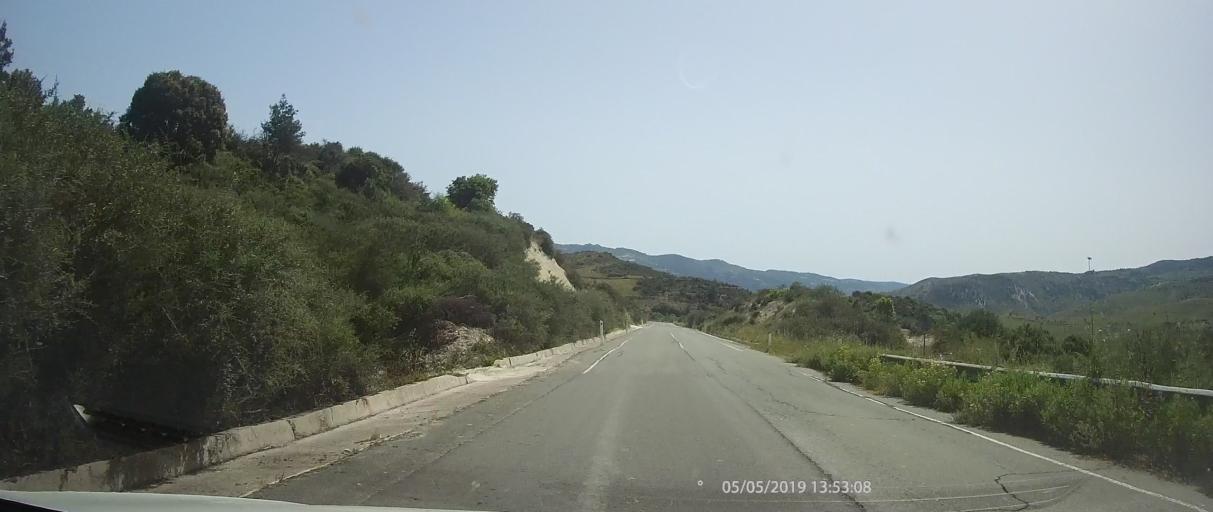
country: CY
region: Limassol
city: Pachna
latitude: 34.8247
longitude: 32.7256
